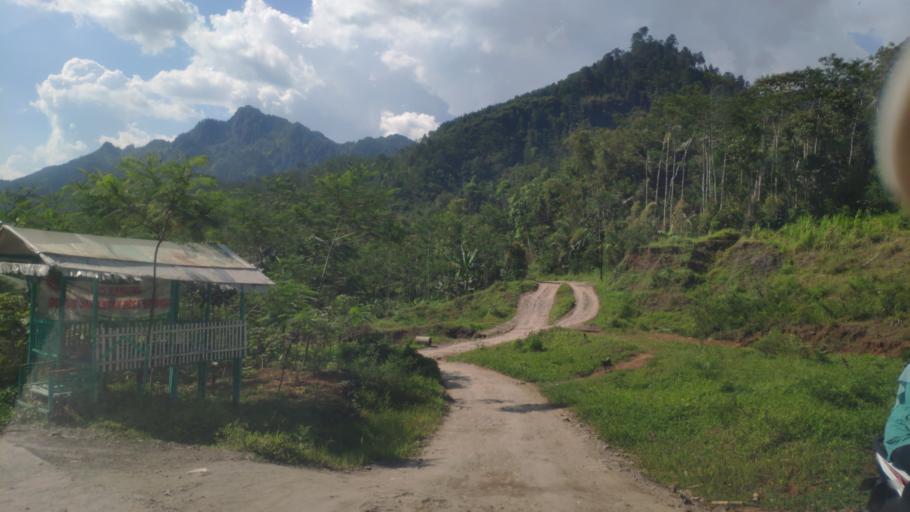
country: ID
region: Central Java
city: Buaran
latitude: -7.2289
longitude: 109.6057
